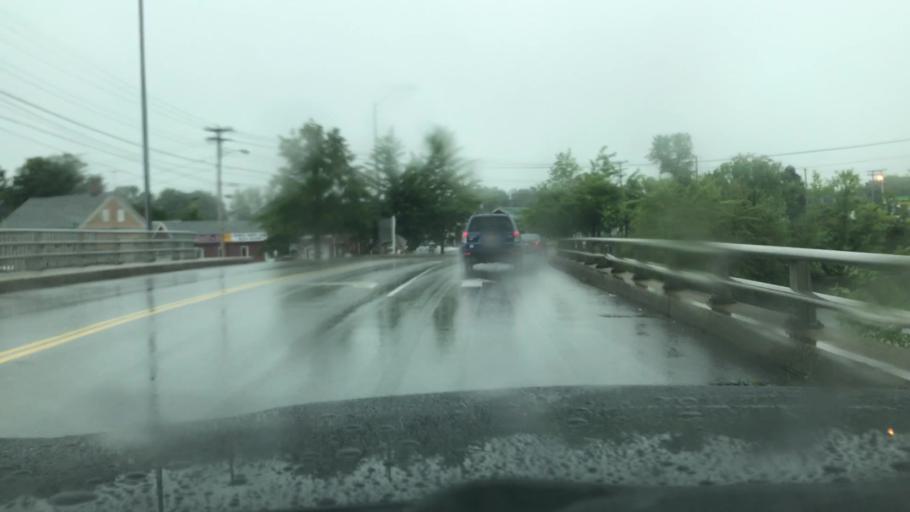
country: US
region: Maine
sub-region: York County
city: Biddeford
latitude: 43.4976
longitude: -70.4552
